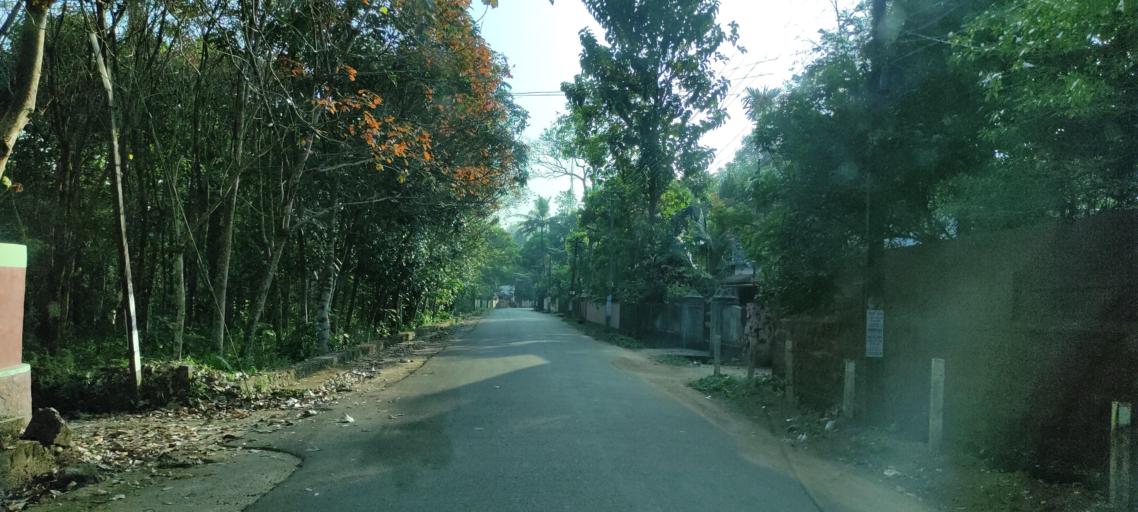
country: IN
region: Kerala
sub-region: Pattanamtitta
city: Adur
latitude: 9.1454
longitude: 76.7454
